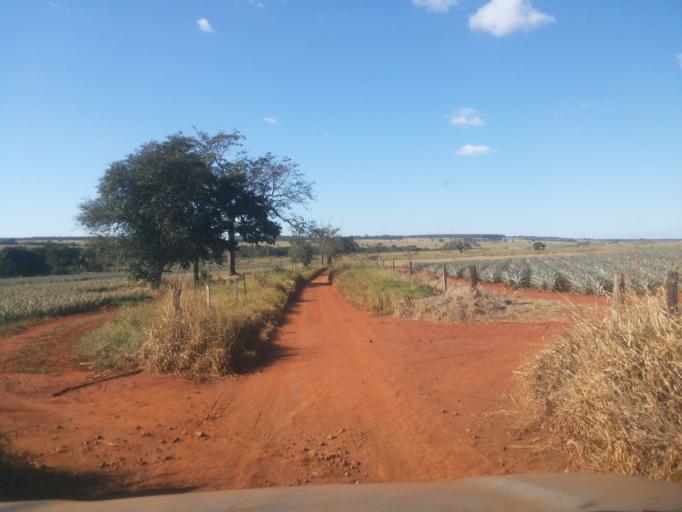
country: BR
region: Minas Gerais
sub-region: Centralina
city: Centralina
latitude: -18.7386
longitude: -49.1838
